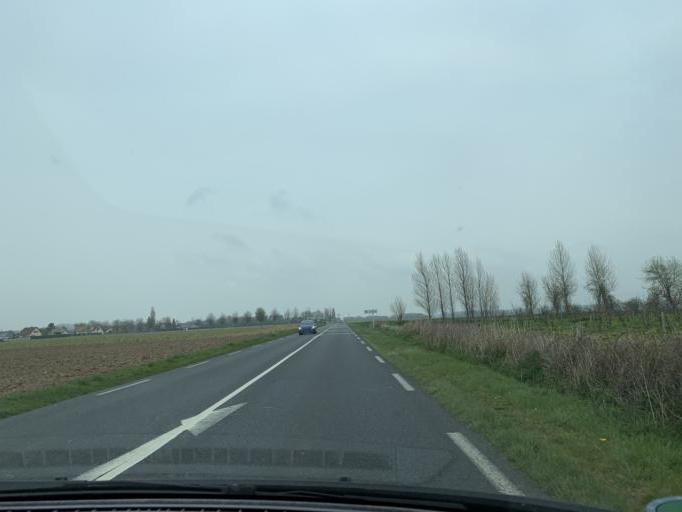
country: FR
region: Haute-Normandie
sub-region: Departement de la Seine-Maritime
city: Martin-Eglise
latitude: 49.9195
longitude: 1.1333
